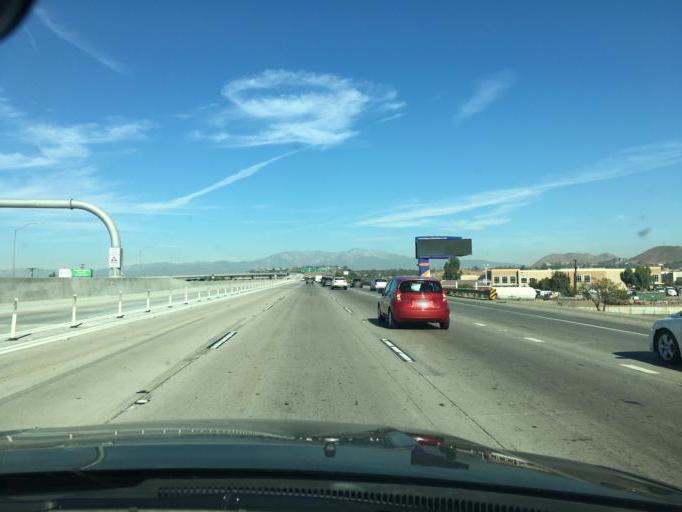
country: US
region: California
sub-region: Riverside County
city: Corona
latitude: 33.8716
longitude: -117.5445
